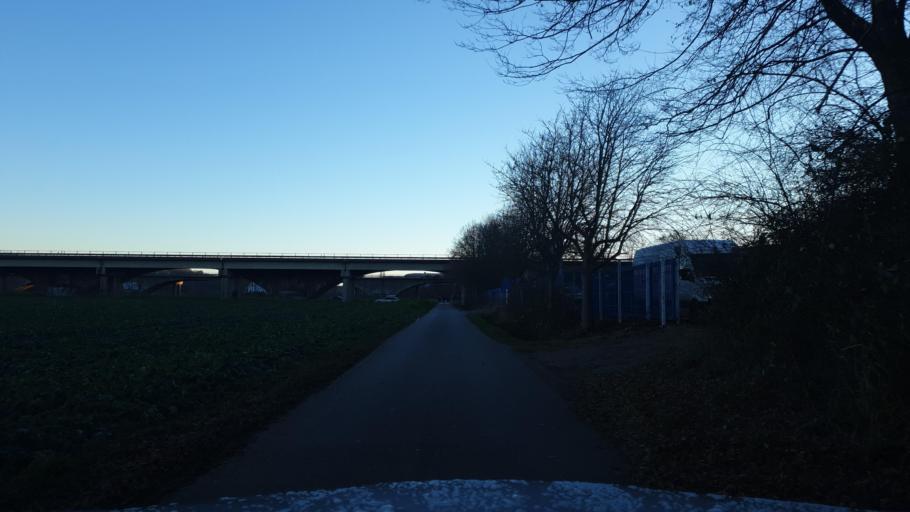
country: DE
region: North Rhine-Westphalia
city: Bad Oeynhausen
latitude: 52.2081
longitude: 8.8456
